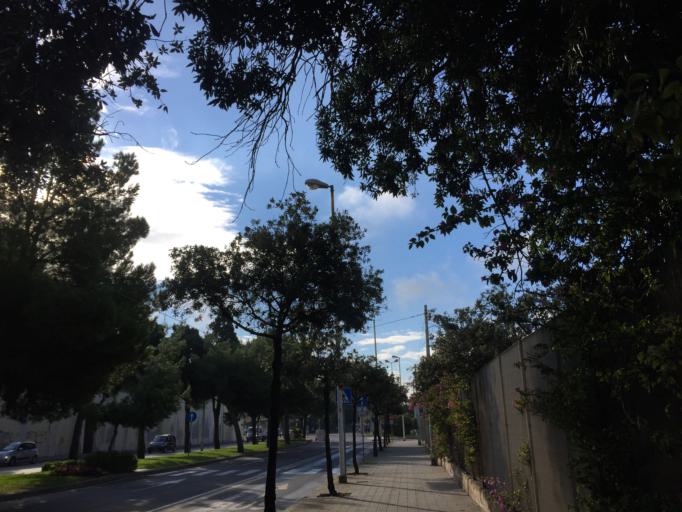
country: IT
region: Sardinia
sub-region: Provincia di Cagliari
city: Cagliari
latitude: 39.2110
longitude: 9.1230
